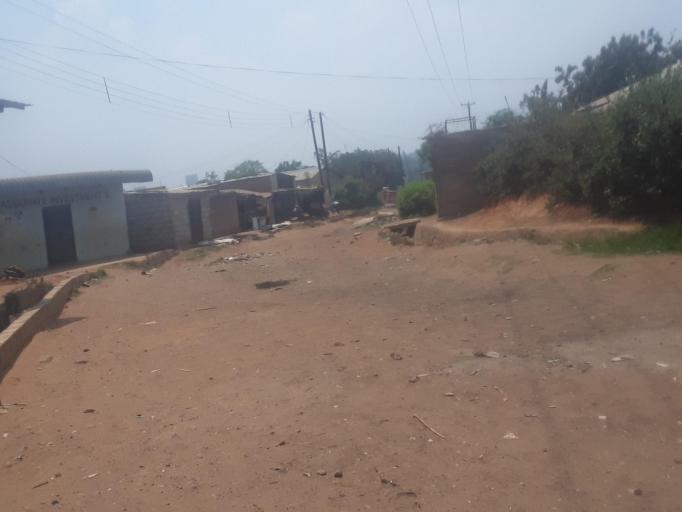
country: ZM
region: Lusaka
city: Lusaka
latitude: -15.3675
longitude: 28.2956
